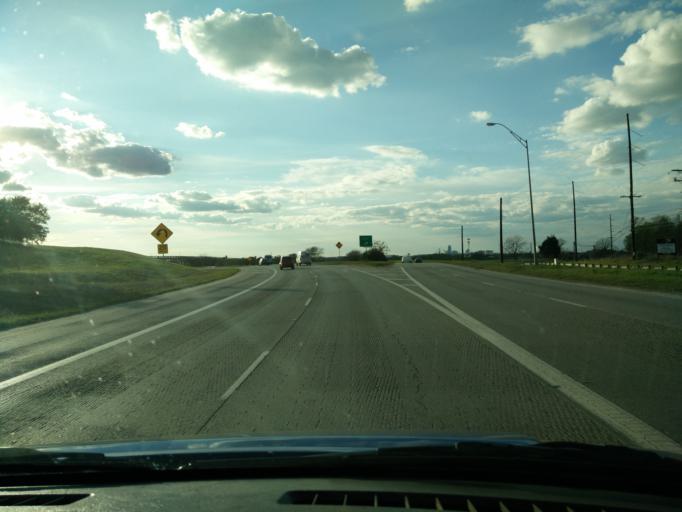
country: US
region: Texas
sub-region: Travis County
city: Austin
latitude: 30.2229
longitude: -97.6778
